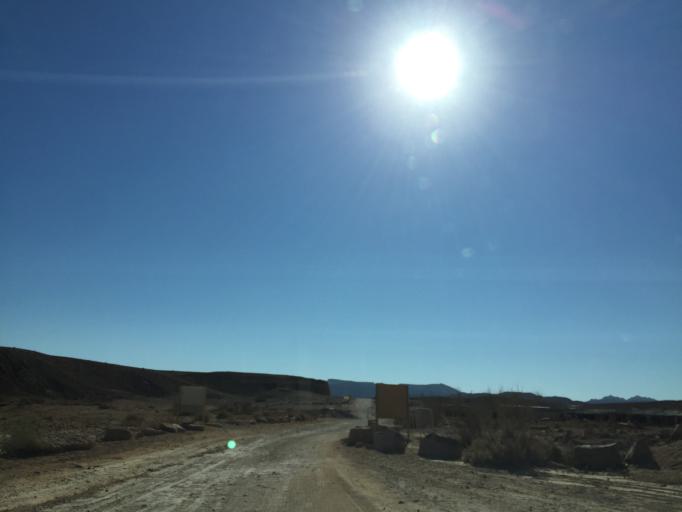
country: IL
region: Southern District
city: Mitzpe Ramon
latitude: 30.6216
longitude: 34.9211
